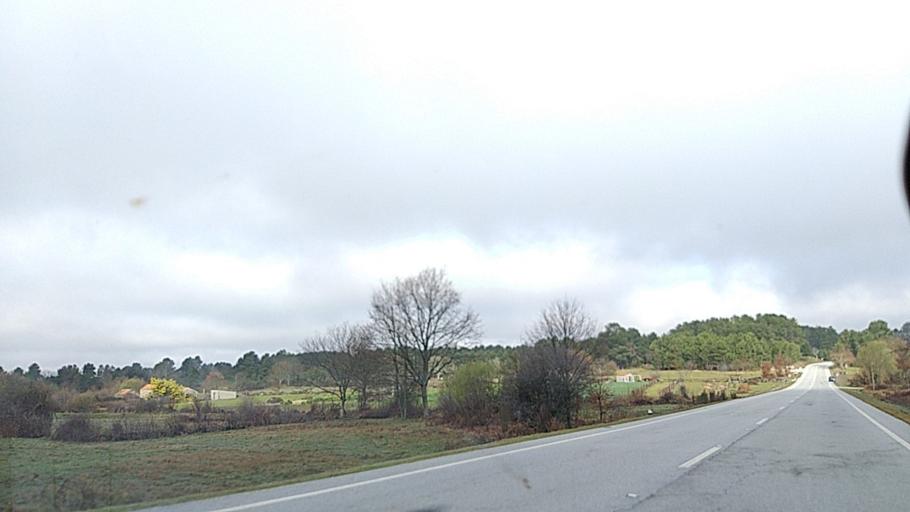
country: PT
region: Guarda
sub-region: Aguiar da Beira
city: Aguiar da Beira
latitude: 40.7456
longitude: -7.5014
